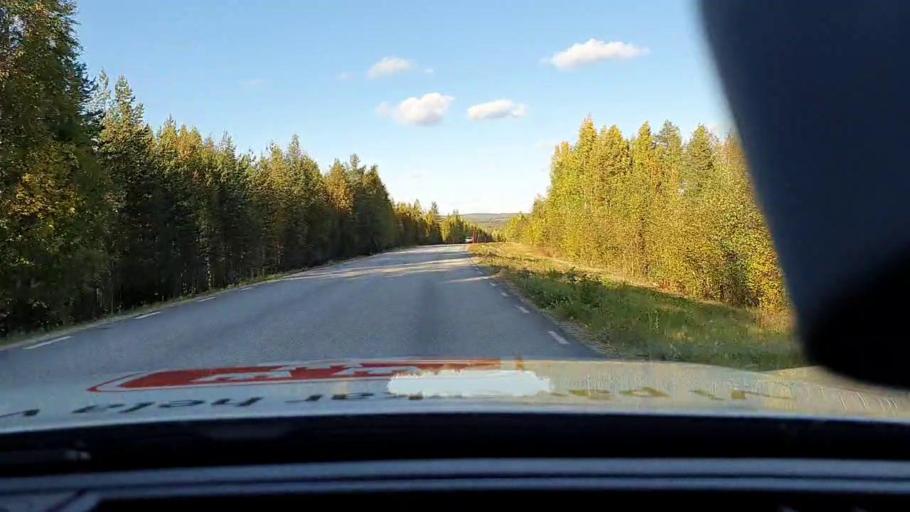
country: SE
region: Norrbotten
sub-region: Pitea Kommun
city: Norrfjarden
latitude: 65.5029
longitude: 21.4775
